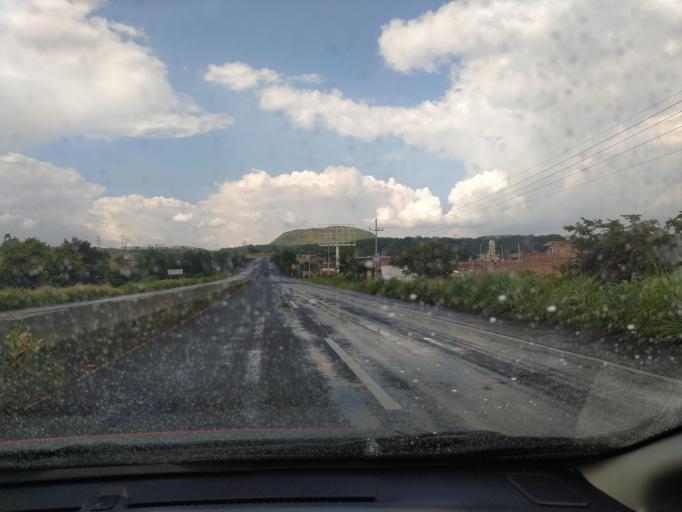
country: MX
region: Jalisco
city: Bellavista
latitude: 20.4265
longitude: -103.6054
